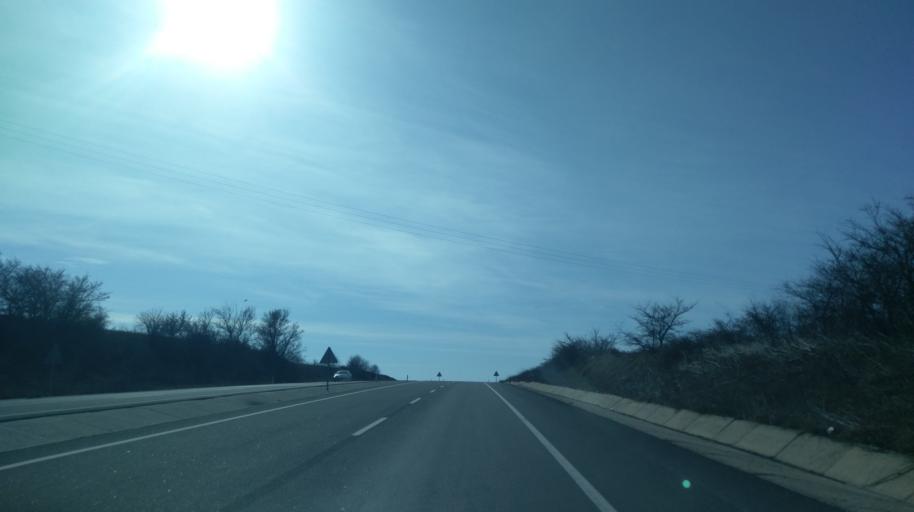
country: TR
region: Edirne
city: Hamidiye
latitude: 41.0966
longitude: 26.6394
